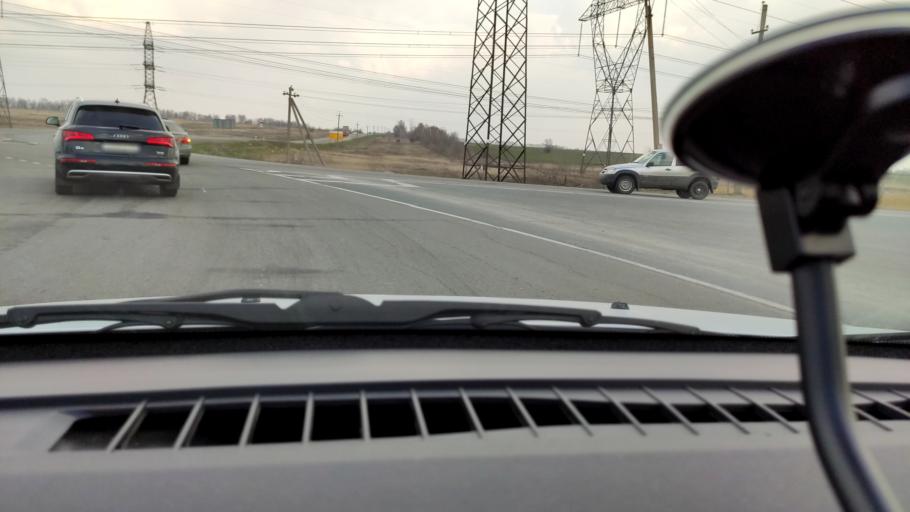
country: RU
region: Samara
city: Dubovyy Umet
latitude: 53.0623
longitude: 50.3763
